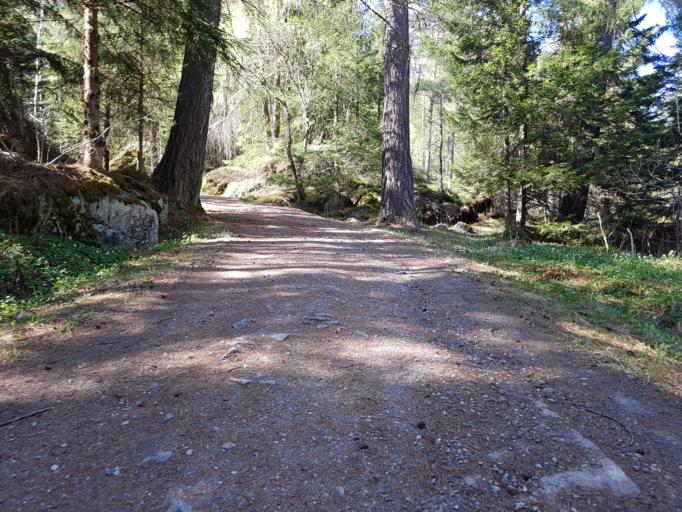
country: NO
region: Sor-Trondelag
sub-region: Trondheim
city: Trondheim
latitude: 63.4383
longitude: 10.3413
